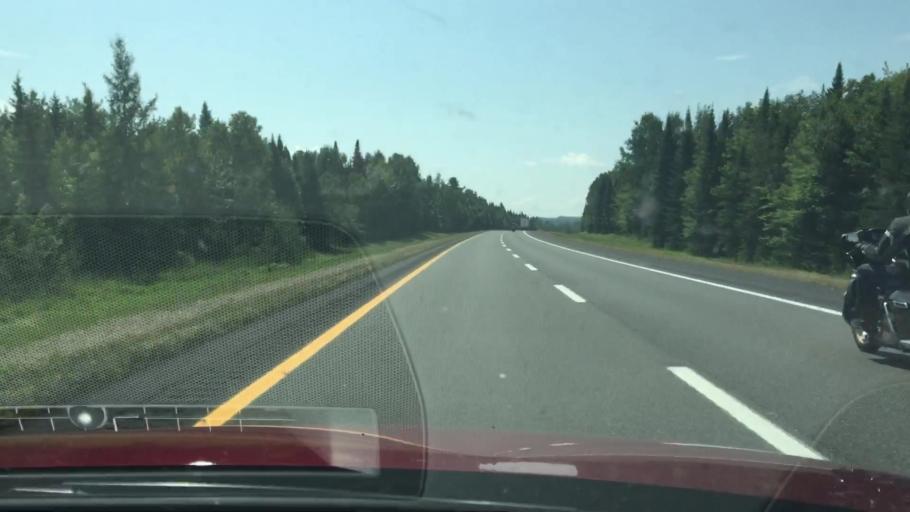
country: US
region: Maine
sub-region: Penobscot County
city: Patten
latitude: 45.9738
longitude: -68.2961
